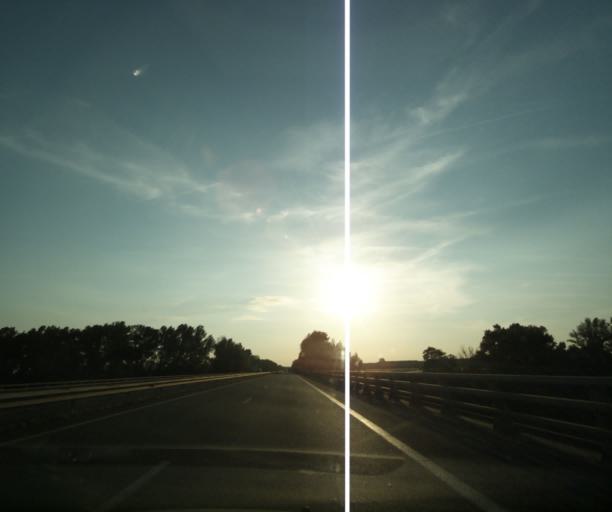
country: FR
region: Midi-Pyrenees
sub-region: Departement du Tarn-et-Garonne
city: Castelsarrasin
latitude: 44.0445
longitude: 1.0649
